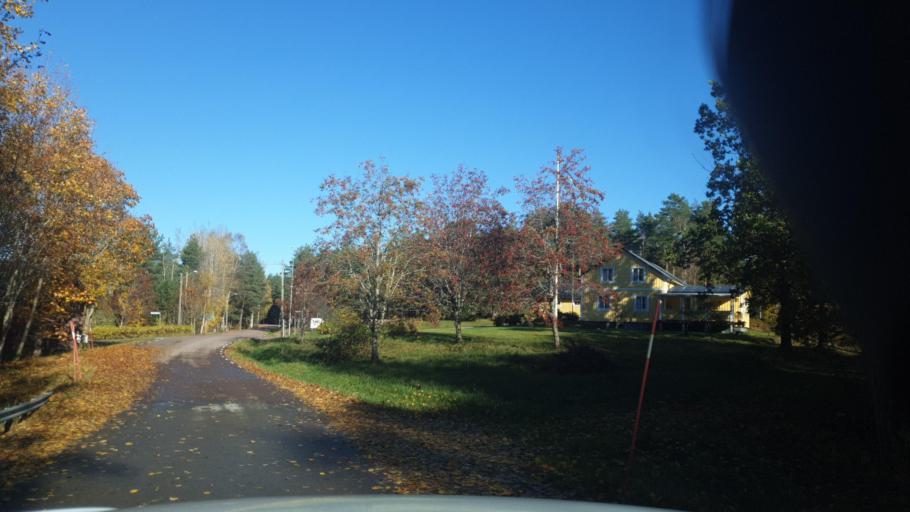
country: SE
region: Vaermland
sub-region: Arvika Kommun
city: Arvika
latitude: 59.5299
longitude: 12.7416
